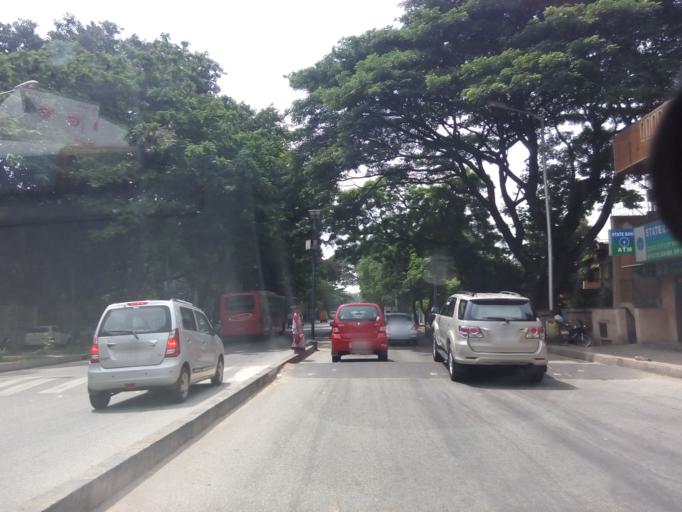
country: IN
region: Karnataka
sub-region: Bangalore Urban
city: Bangalore
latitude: 12.9258
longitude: 77.6250
